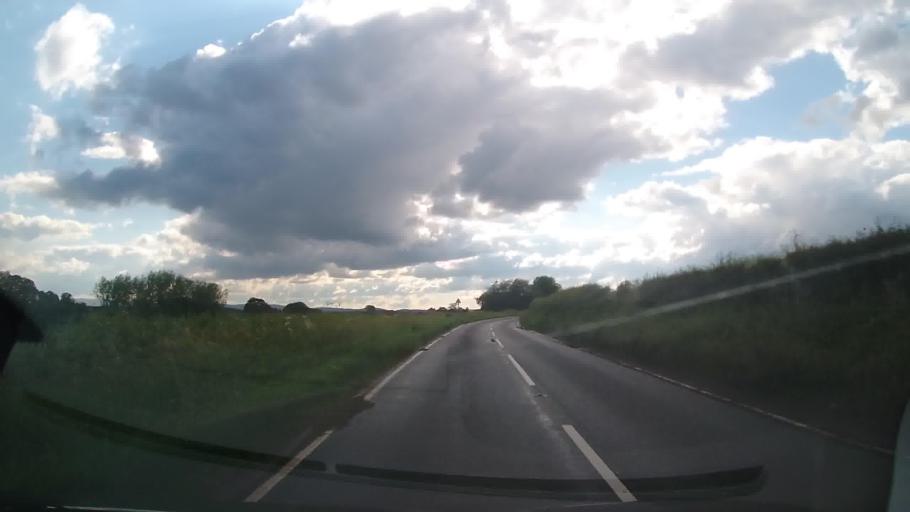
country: GB
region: England
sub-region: Shropshire
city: Withington
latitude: 52.6709
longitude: -2.6370
